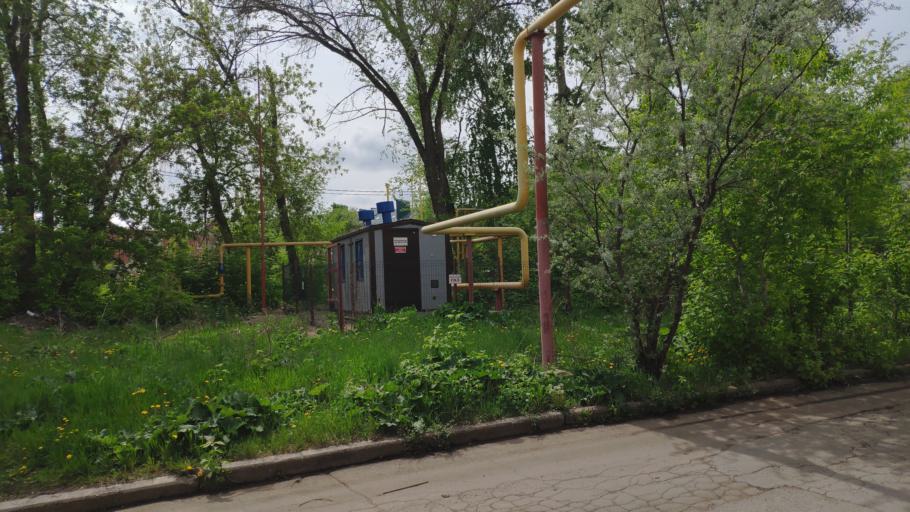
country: RU
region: Chelyabinsk
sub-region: Gorod Magnitogorsk
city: Magnitogorsk
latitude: 53.4190
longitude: 58.9562
